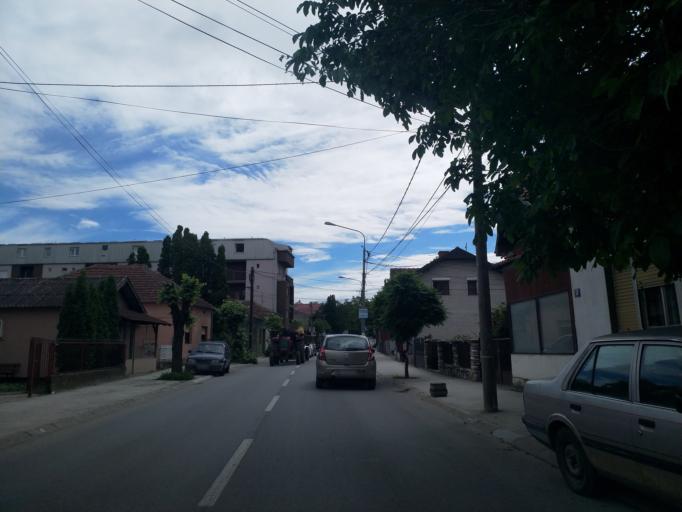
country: RS
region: Central Serbia
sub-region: Pomoravski Okrug
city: Jagodina
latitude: 43.9739
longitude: 21.2554
